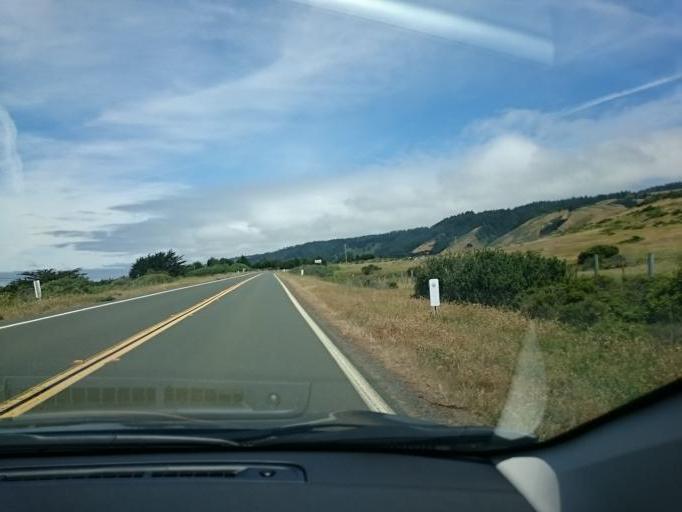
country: US
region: California
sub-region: Mendocino County
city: Fort Bragg
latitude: 39.1198
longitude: -123.7156
